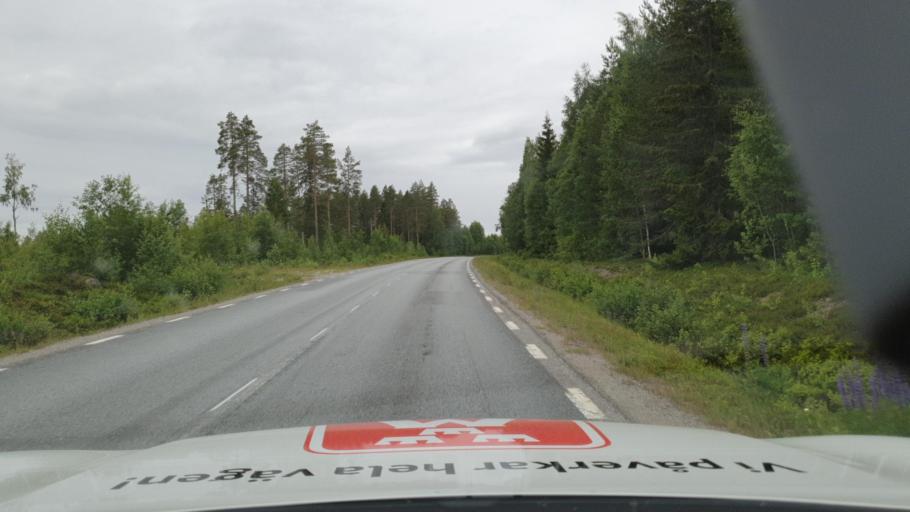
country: SE
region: Vaesterbotten
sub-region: Vannas Kommun
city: Vaennaes
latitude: 63.7742
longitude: 19.7234
